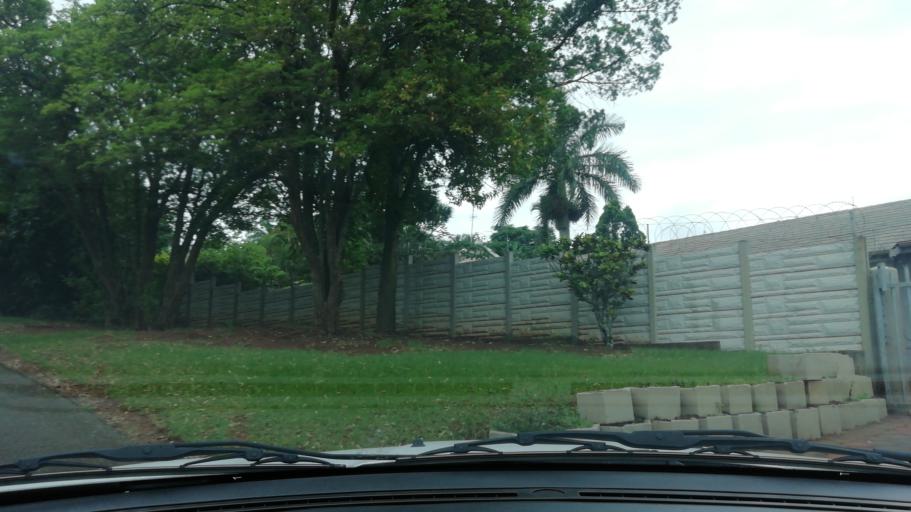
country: ZA
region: KwaZulu-Natal
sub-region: uThungulu District Municipality
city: Empangeni
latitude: -28.7573
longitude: 31.8877
